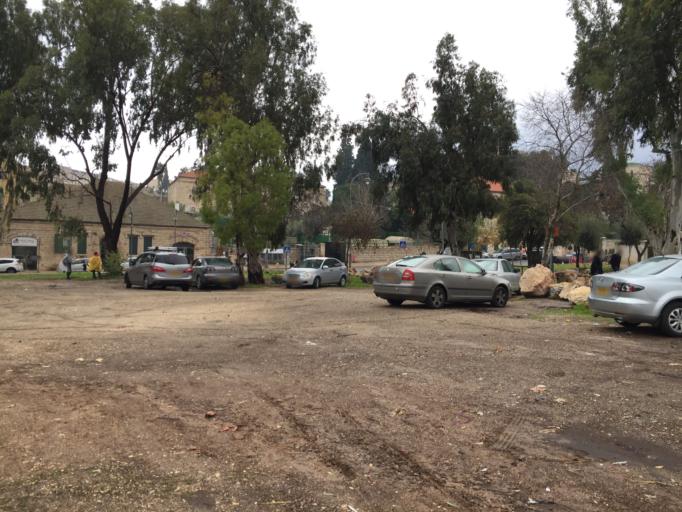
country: IL
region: Jerusalem
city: West Jerusalem
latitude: 31.7775
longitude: 35.2202
